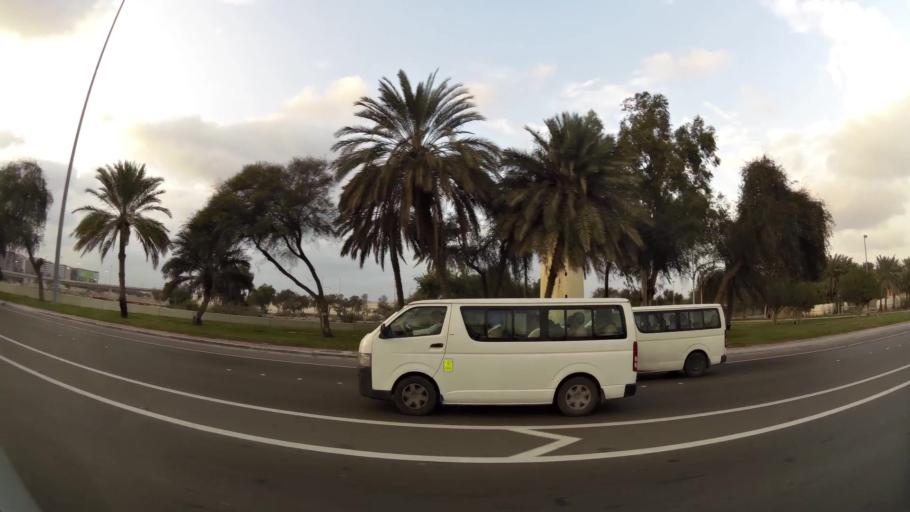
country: AE
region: Abu Dhabi
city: Abu Dhabi
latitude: 24.4201
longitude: 54.4814
